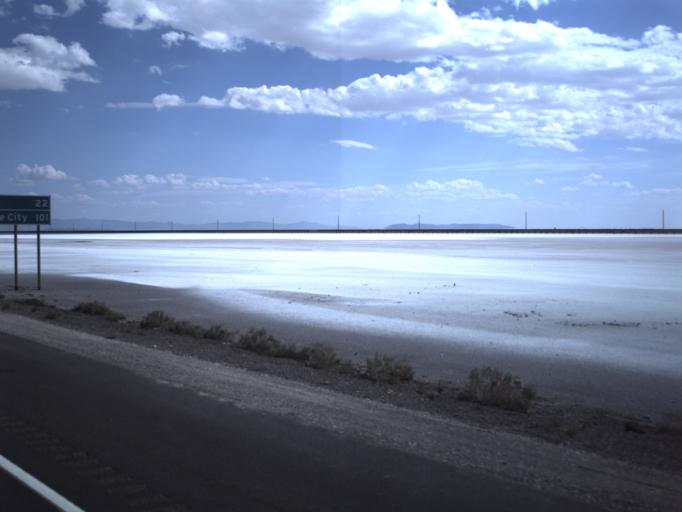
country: US
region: Utah
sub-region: Tooele County
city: Wendover
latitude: 40.7342
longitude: -113.6477
